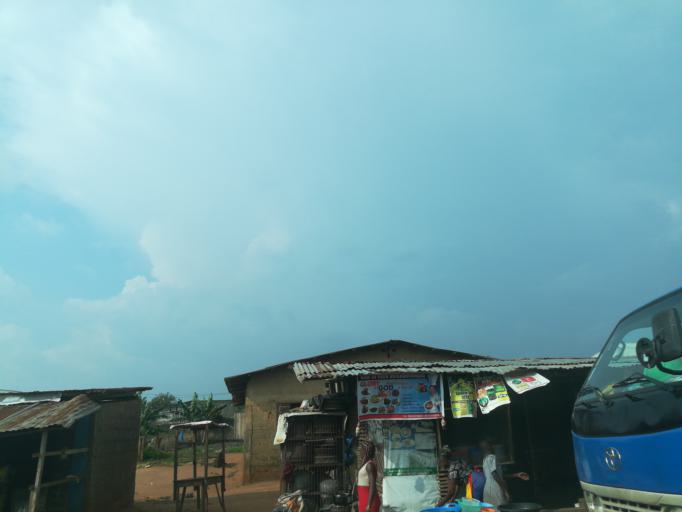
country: NG
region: Lagos
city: Ikorodu
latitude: 6.6611
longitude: 3.6689
